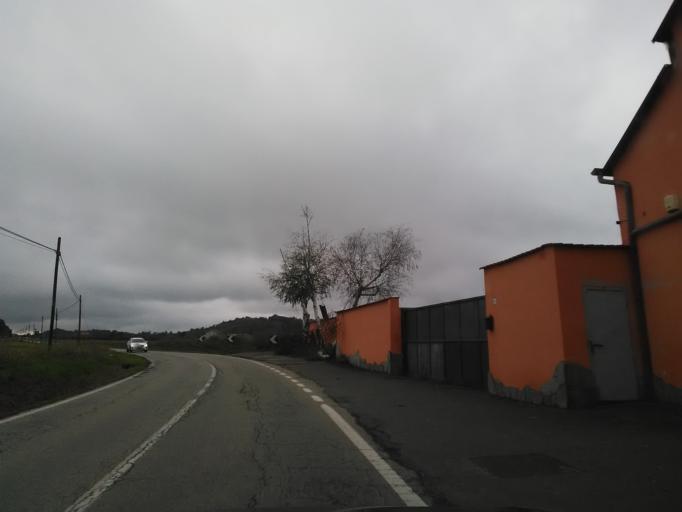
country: IT
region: Piedmont
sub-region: Provincia di Vercelli
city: Cigliano
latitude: 45.3114
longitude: 8.0020
